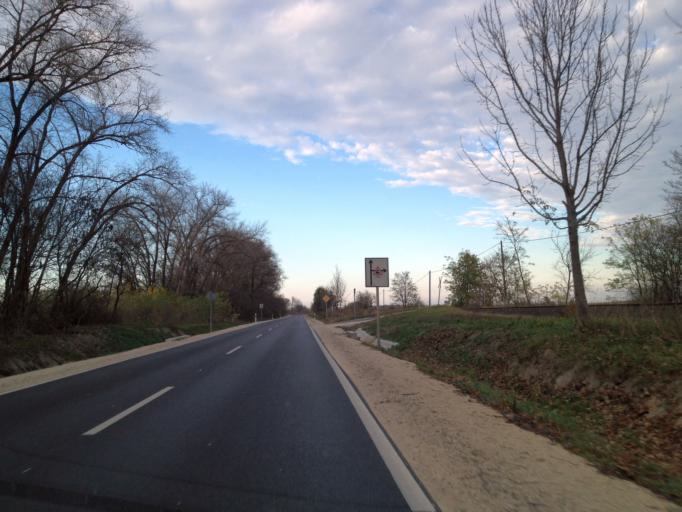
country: HU
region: Gyor-Moson-Sopron
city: Nyul
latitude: 47.6005
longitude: 17.6878
